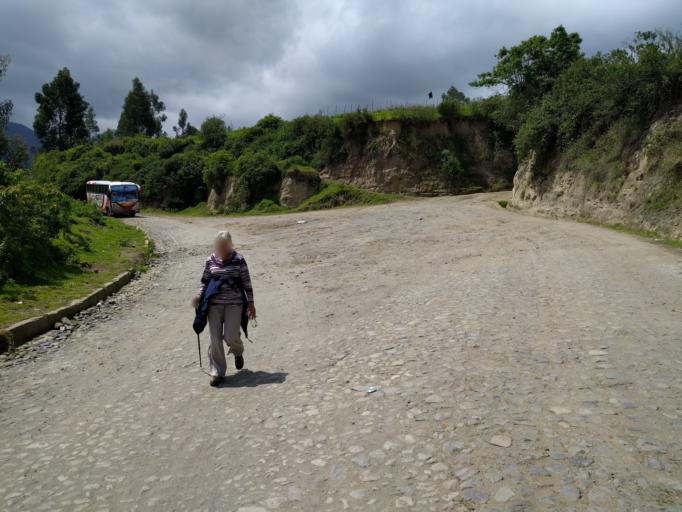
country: EC
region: Imbabura
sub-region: Canton Otavalo
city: Otavalo
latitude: 0.1990
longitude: -78.2741
